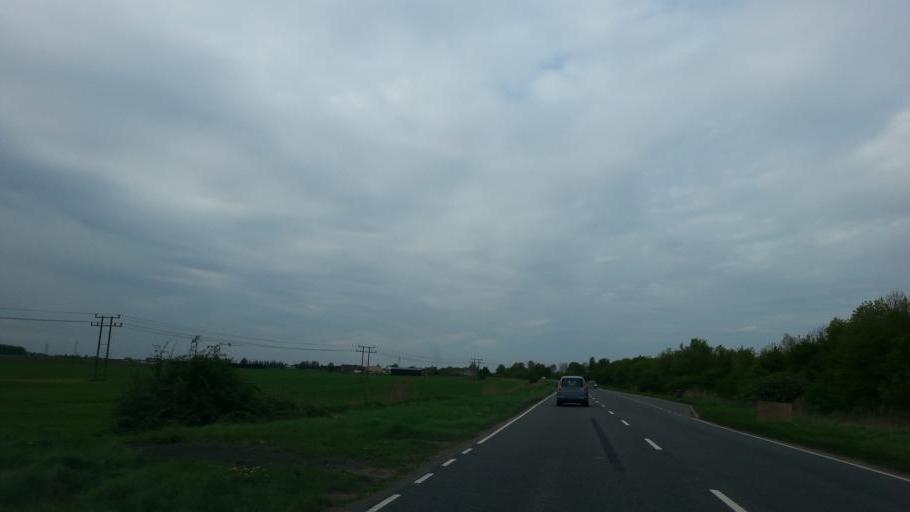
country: GB
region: England
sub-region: Cambridgeshire
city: March
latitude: 52.5389
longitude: 0.0699
